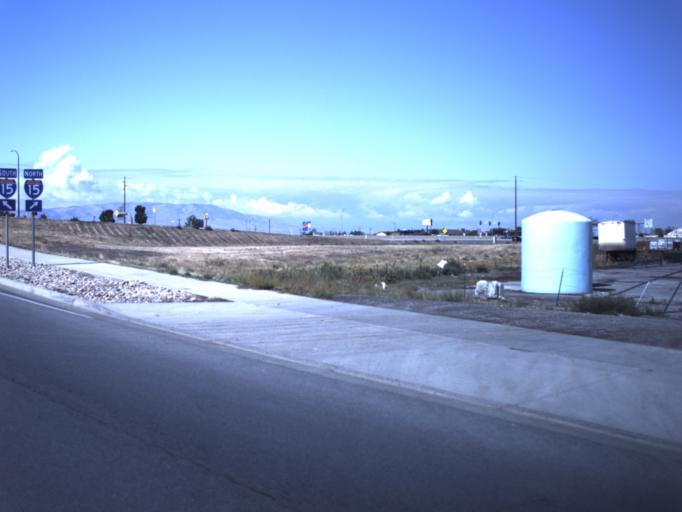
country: US
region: Utah
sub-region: Utah County
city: Springville
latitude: 40.1614
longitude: -111.6437
